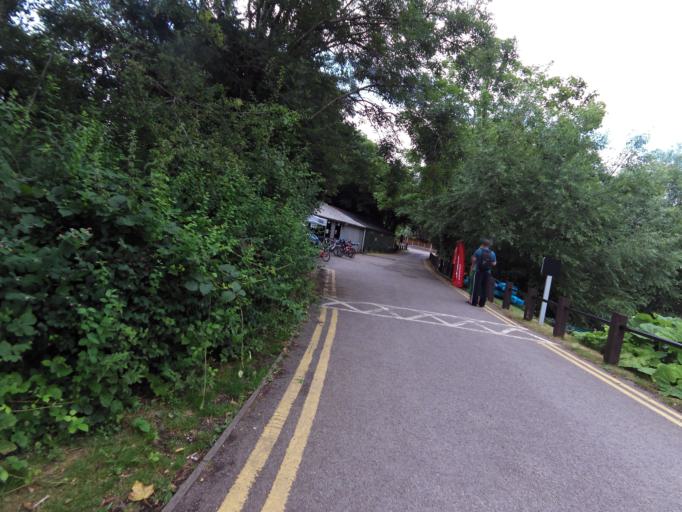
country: GB
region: England
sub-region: Hertfordshire
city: Broxbourne
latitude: 51.7432
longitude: -0.0143
